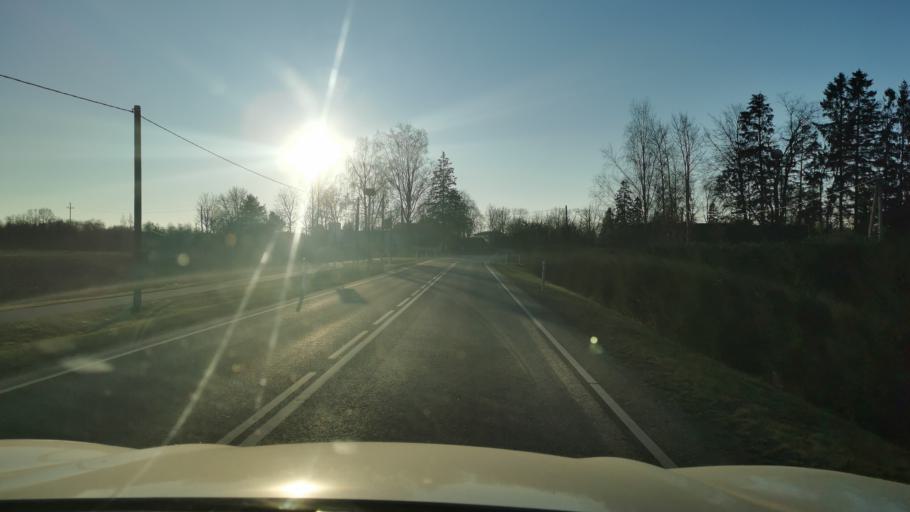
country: EE
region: Ida-Virumaa
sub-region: Kivioli linn
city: Kivioli
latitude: 59.3224
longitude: 27.0112
